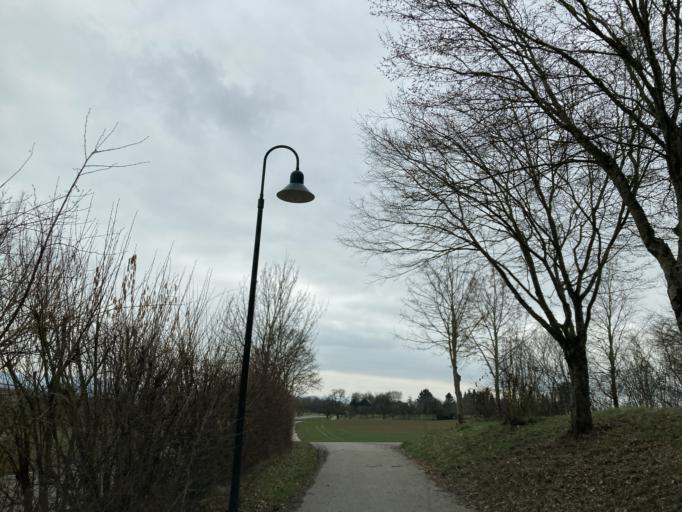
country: DE
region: Baden-Wuerttemberg
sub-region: Tuebingen Region
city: Hirrlingen
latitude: 48.4306
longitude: 8.8489
